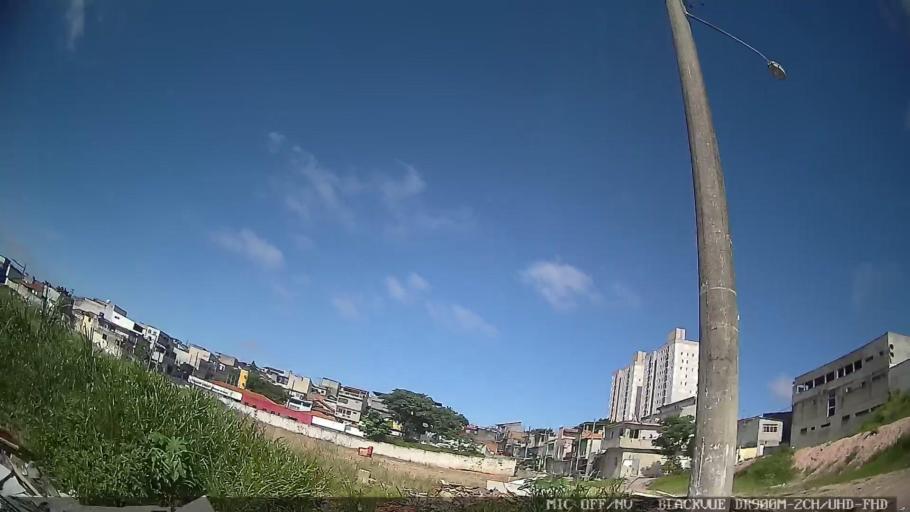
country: BR
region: Sao Paulo
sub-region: Itaquaquecetuba
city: Itaquaquecetuba
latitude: -23.4972
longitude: -46.3405
